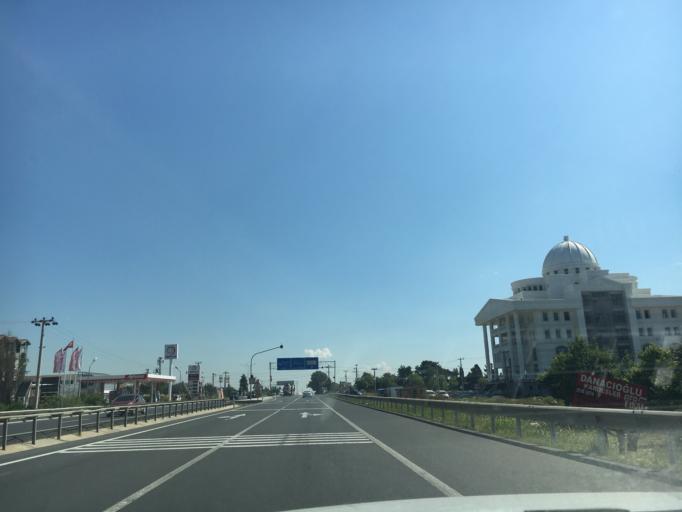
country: TR
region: Tekirdag
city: Marmara Ereglisi
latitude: 40.9761
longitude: 27.9512
